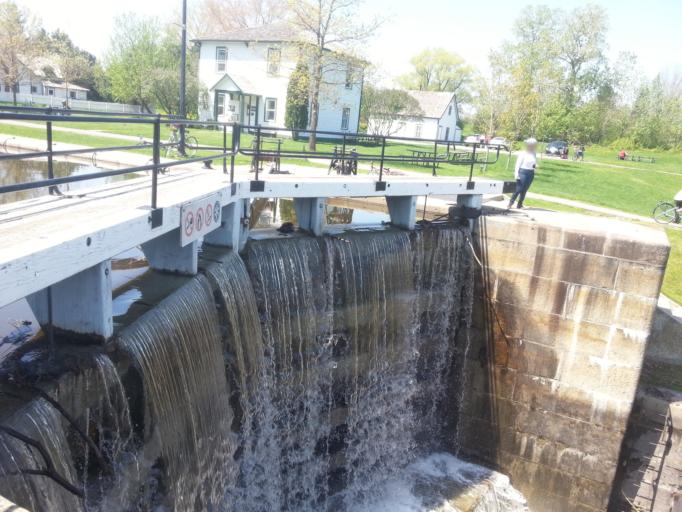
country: CA
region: Ontario
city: Ottawa
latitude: 45.3844
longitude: -75.6999
